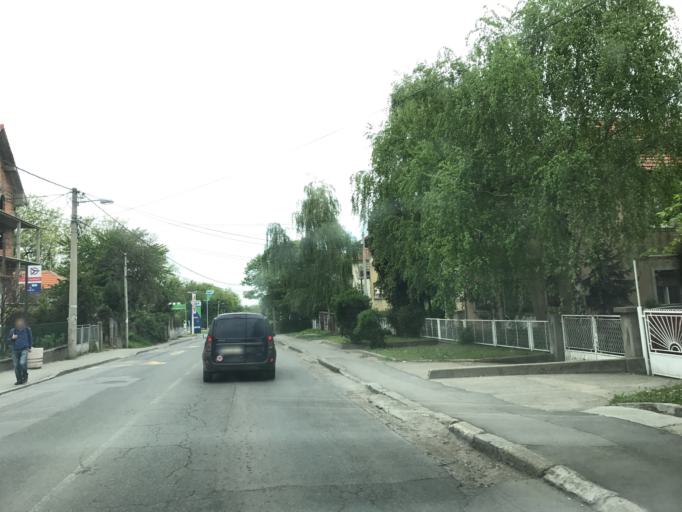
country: RS
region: Central Serbia
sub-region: Belgrade
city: Palilula
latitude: 44.8079
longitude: 20.5143
